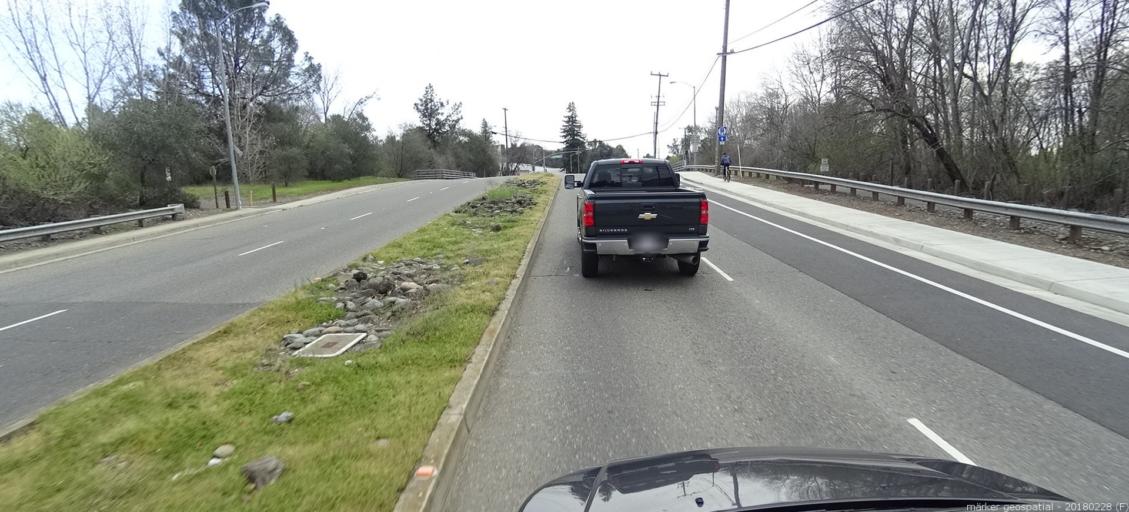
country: US
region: California
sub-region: Sacramento County
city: Folsom
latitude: 38.6579
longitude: -121.1691
